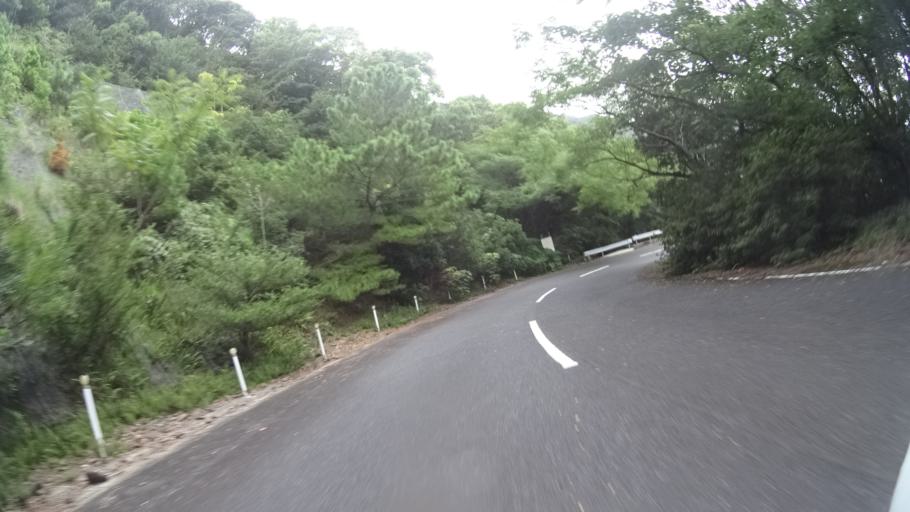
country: JP
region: Kagoshima
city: Nishinoomote
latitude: 30.3198
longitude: 130.3996
